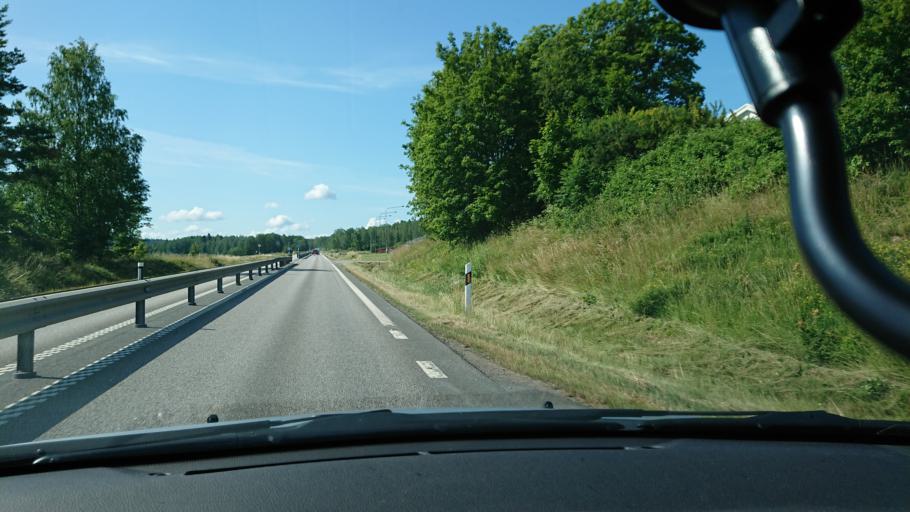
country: SE
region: OEstergoetland
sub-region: Kinda Kommun
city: Rimforsa
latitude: 58.1311
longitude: 15.6764
